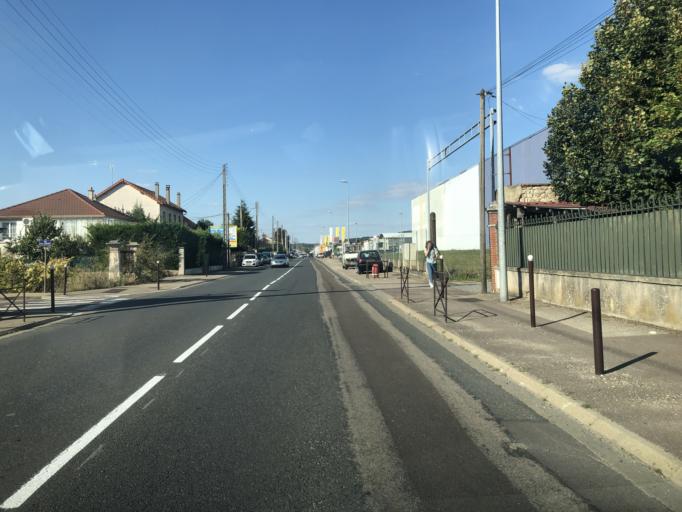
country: FR
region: Bourgogne
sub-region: Departement de l'Yonne
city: Auxerre
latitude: 47.8026
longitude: 3.5819
